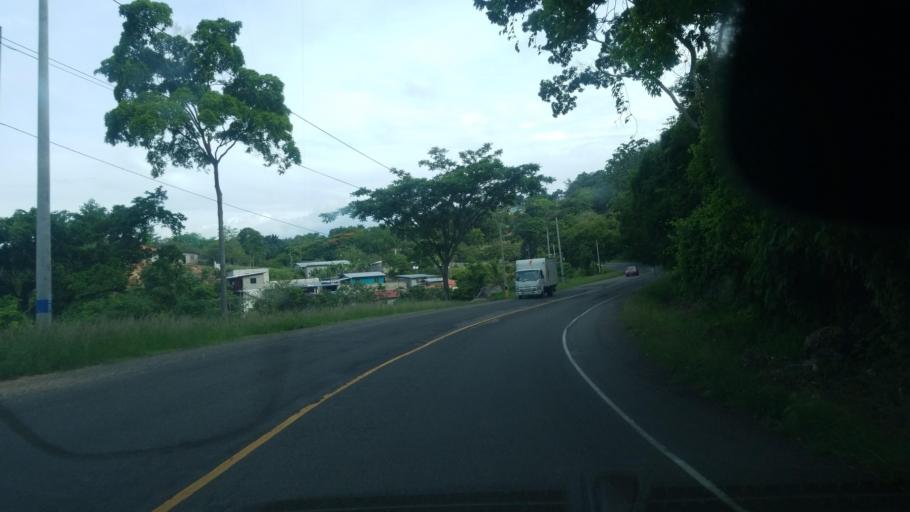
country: HN
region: Santa Barbara
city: Trinidad
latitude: 15.1583
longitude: -88.2605
